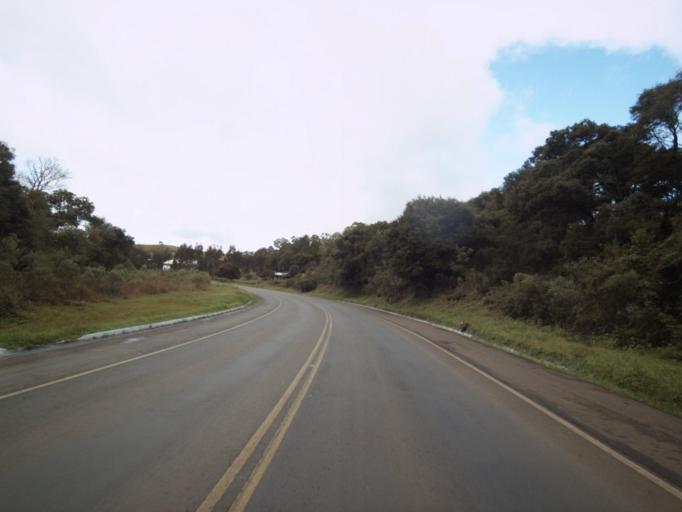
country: BR
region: Santa Catarina
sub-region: Concordia
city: Concordia
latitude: -27.0868
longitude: -51.9114
